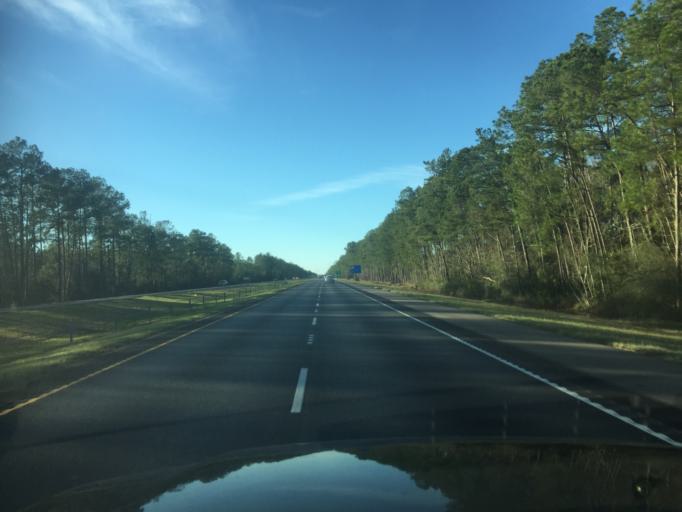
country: US
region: Louisiana
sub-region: Saint Tammany Parish
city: Lacombe
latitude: 30.3439
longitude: -89.9043
